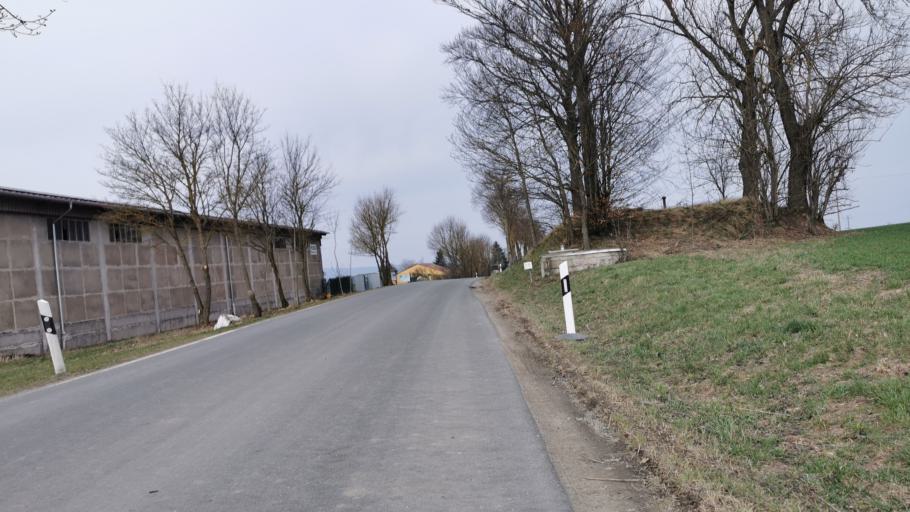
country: DE
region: Thuringia
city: Leutenberg
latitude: 50.5351
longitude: 11.4288
